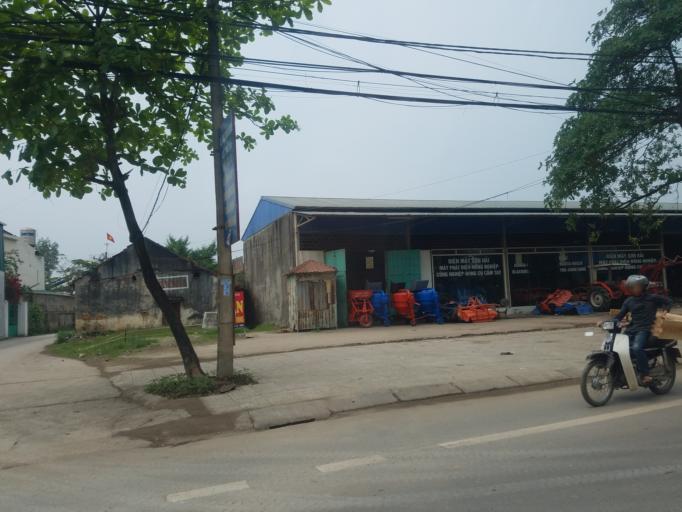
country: VN
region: Thai Nguyen
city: Chua Hang
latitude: 21.6098
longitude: 105.8396
